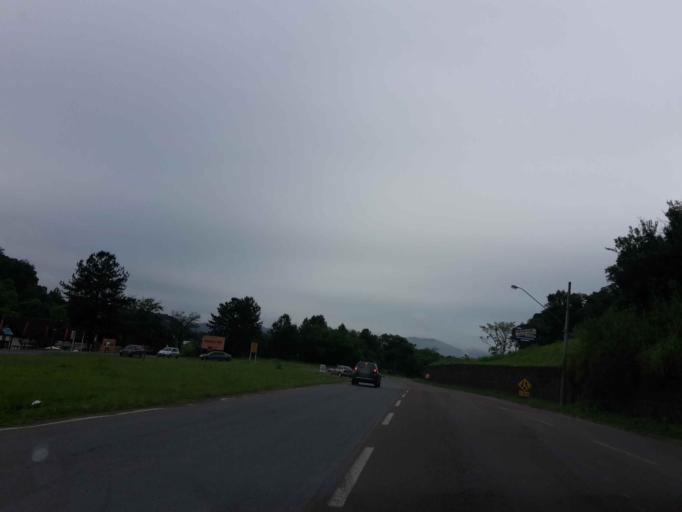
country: BR
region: Santa Catarina
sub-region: Blumenau
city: Blumenau
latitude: -26.8654
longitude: -49.0999
